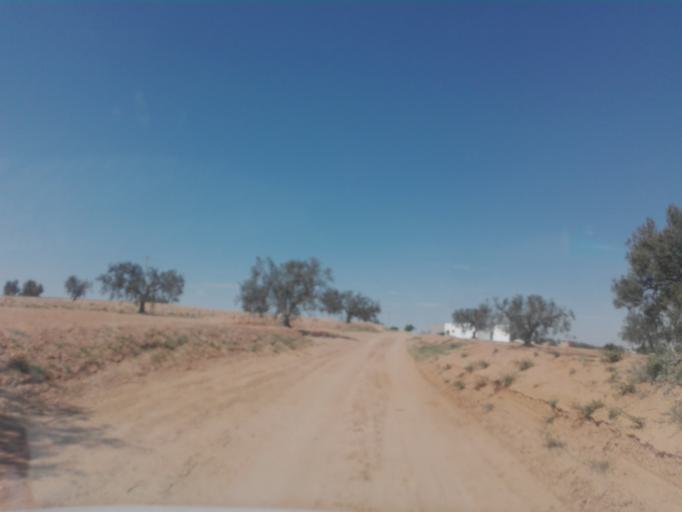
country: TN
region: Safaqis
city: Bi'r `Ali Bin Khalifah
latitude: 34.6632
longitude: 10.3106
